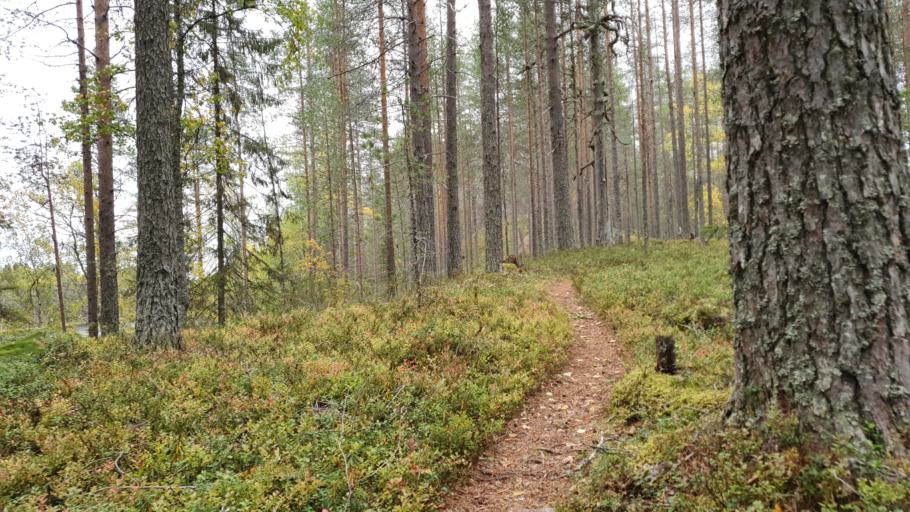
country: FI
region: Kainuu
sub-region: Kehys-Kainuu
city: Kuhmo
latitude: 64.2925
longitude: 29.3248
